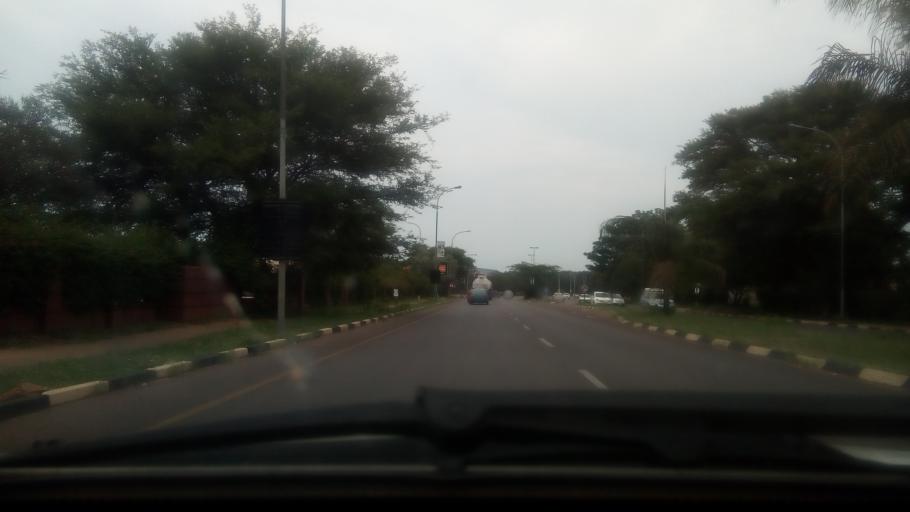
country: BW
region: South East
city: Gaborone
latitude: -24.6636
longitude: 25.9292
